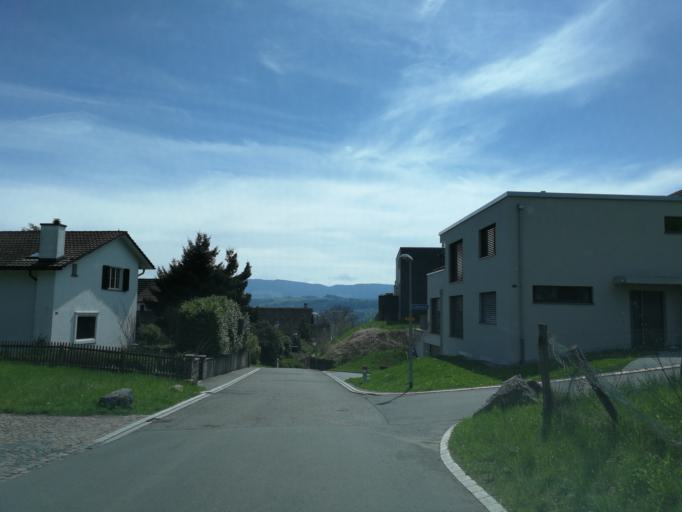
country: CH
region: Zurich
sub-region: Bezirk Meilen
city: Meilen
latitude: 47.2753
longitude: 8.6384
